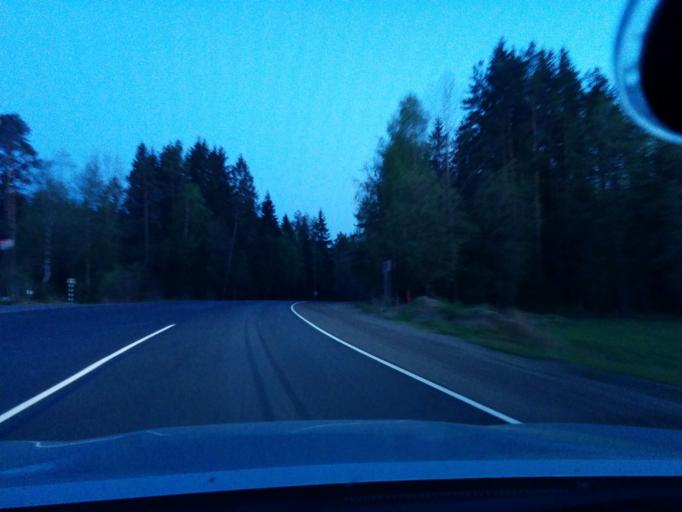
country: RU
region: Leningrad
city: Verkhniye Osel'ki
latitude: 60.1992
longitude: 30.4259
